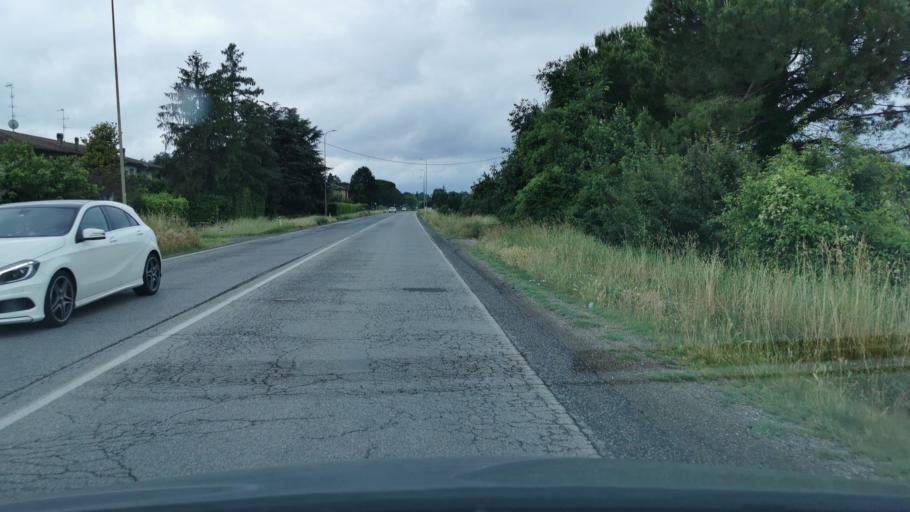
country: IT
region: Emilia-Romagna
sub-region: Provincia di Ravenna
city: Faenza
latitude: 44.3033
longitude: 11.8852
